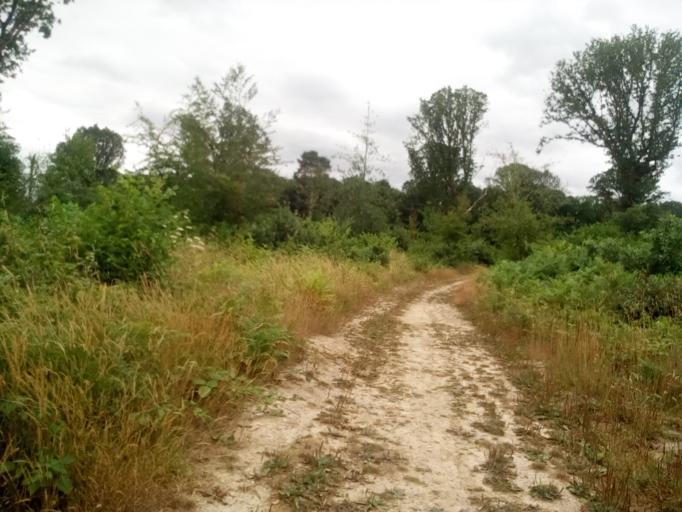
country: FR
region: Lower Normandy
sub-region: Departement du Calvados
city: Clinchamps-sur-Orne
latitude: 49.0437
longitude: -0.4365
